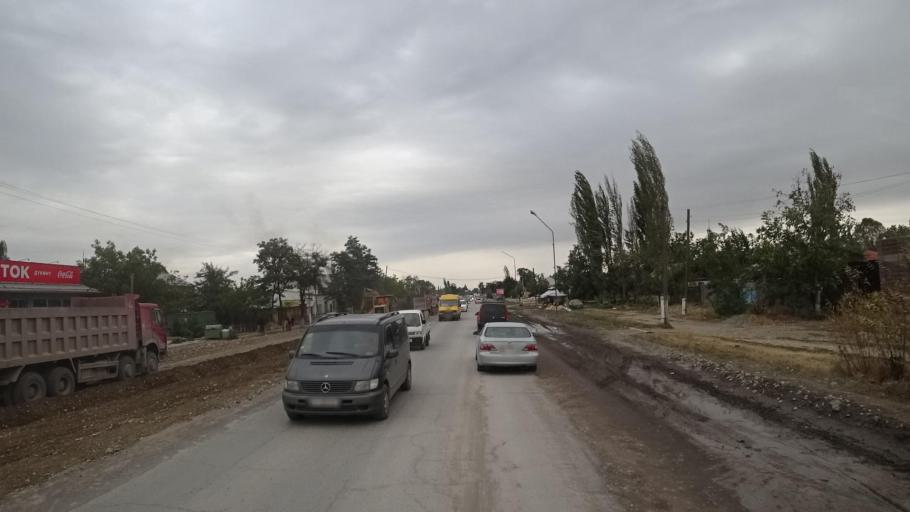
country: KG
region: Chuy
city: Sokuluk
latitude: 42.8544
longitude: 74.2367
